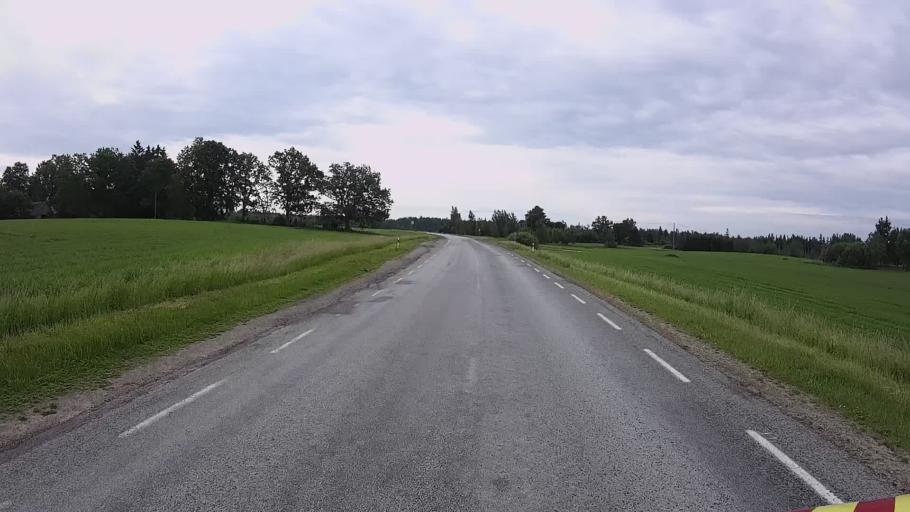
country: EE
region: Viljandimaa
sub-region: Viljandi linn
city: Viljandi
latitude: 58.2312
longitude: 25.6018
